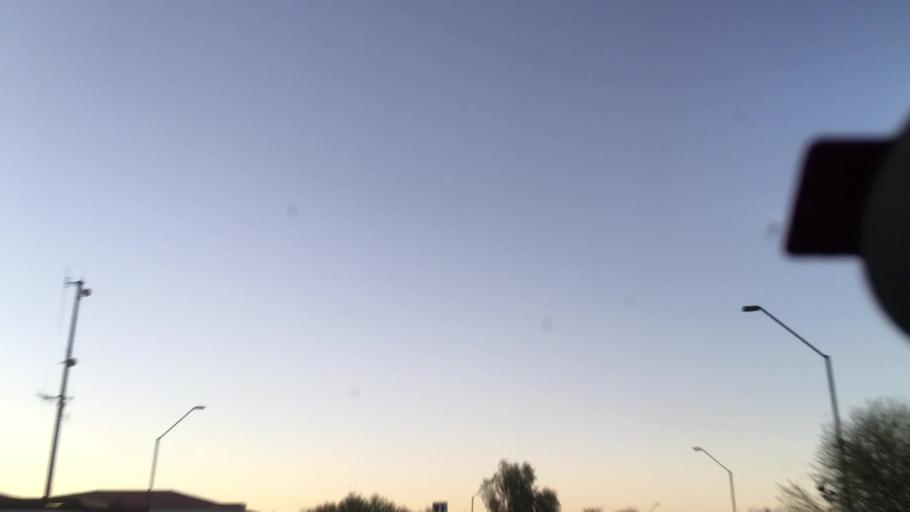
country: US
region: Arizona
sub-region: Maricopa County
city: Peoria
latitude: 33.5736
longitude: -112.2377
